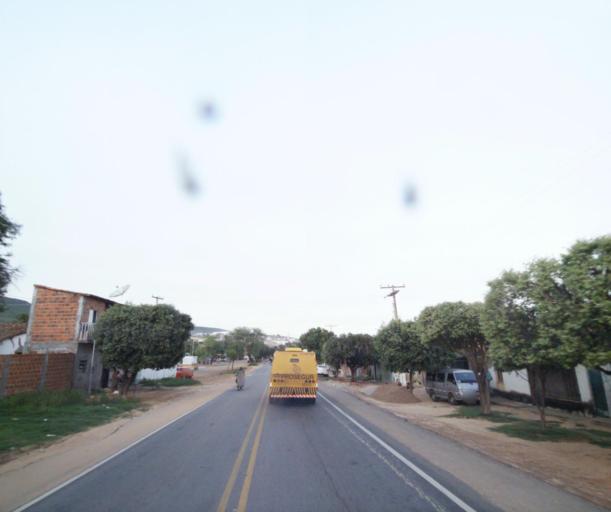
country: BR
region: Bahia
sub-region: Brumado
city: Brumado
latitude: -14.2496
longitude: -41.7336
